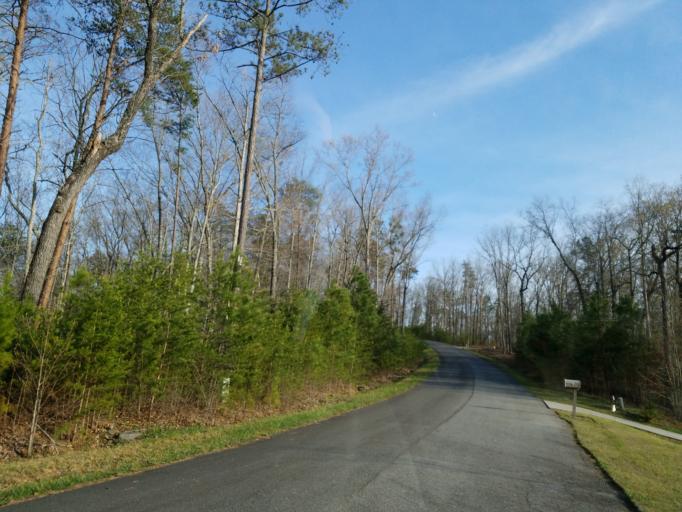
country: US
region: Georgia
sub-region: Pickens County
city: Jasper
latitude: 34.5225
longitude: -84.4579
